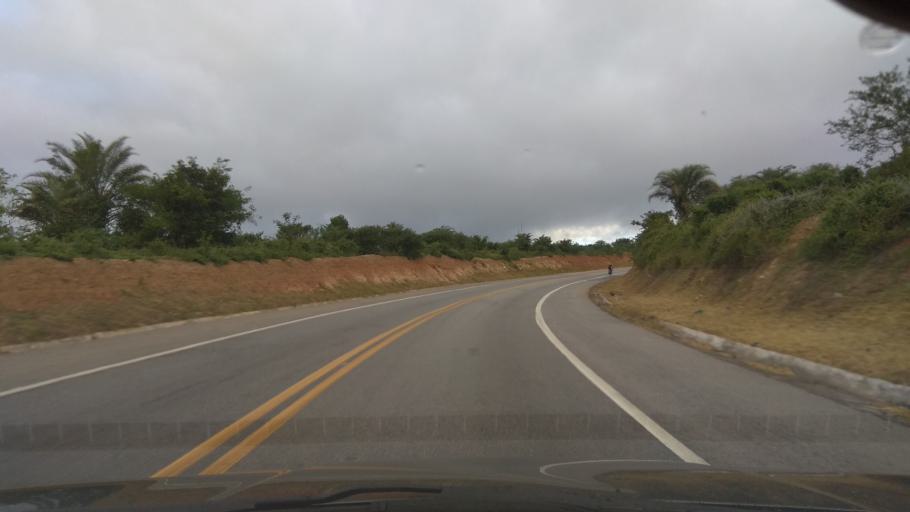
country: BR
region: Bahia
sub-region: Santa Ines
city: Santa Ines
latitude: -13.3135
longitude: -40.0182
